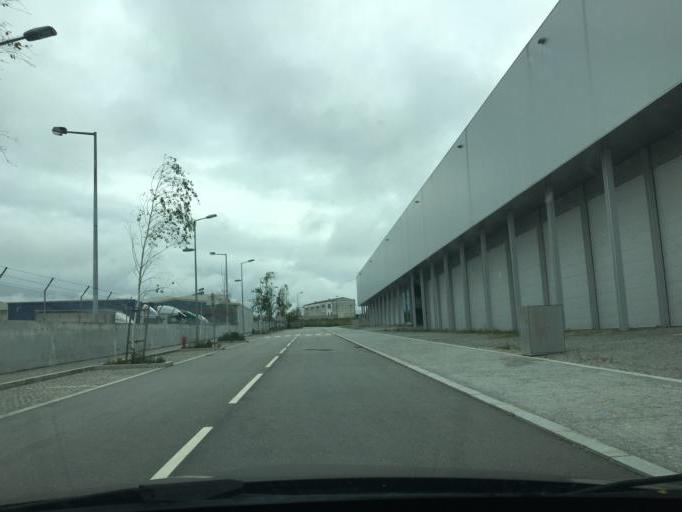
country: PT
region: Porto
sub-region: Matosinhos
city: Santa Cruz do Bispo
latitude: 41.2337
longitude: -8.6649
